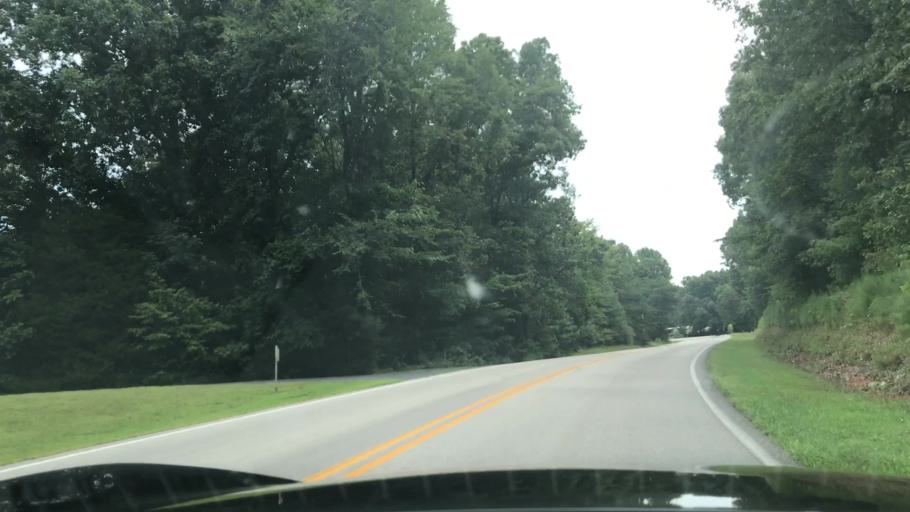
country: US
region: Kentucky
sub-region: Butler County
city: Morgantown
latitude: 37.1844
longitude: -86.8733
